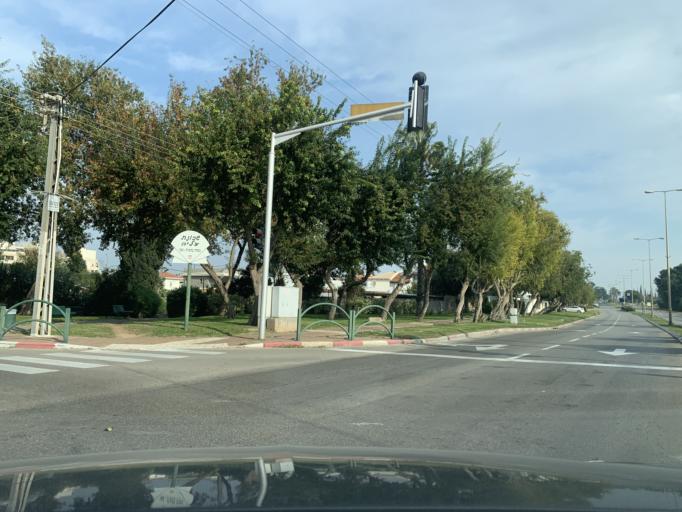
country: IL
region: Central District
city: Kfar Saba
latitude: 32.1877
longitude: 34.9049
